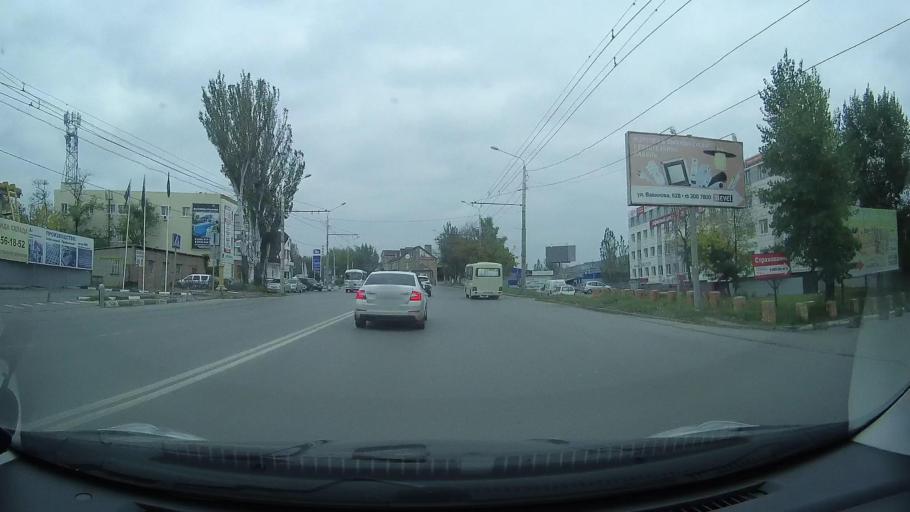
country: RU
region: Rostov
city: Severnyy
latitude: 47.2741
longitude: 39.6863
